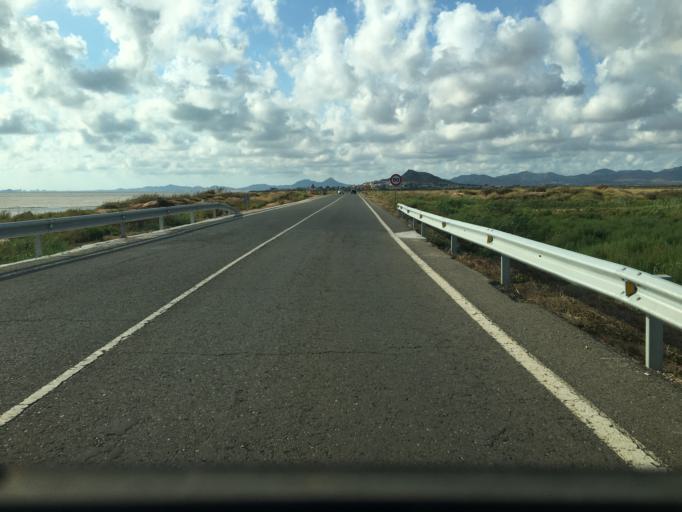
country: ES
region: Murcia
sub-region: Murcia
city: Los Alcazares
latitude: 37.7133
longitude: -0.8578
